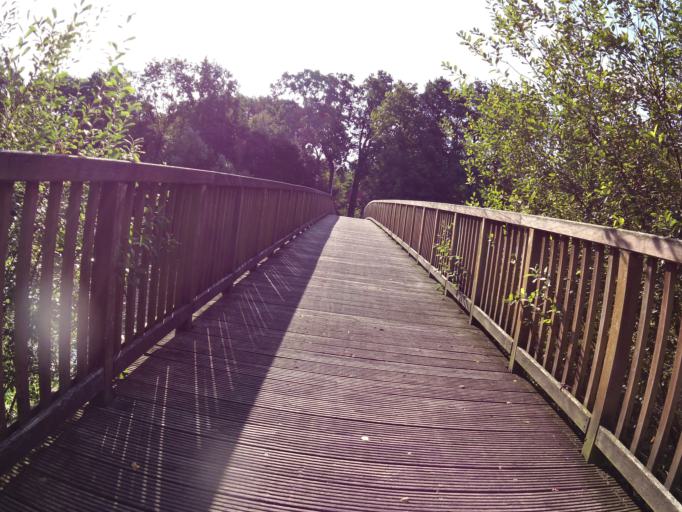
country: DE
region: Lower Saxony
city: Bremervorde
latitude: 53.4811
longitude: 9.1549
